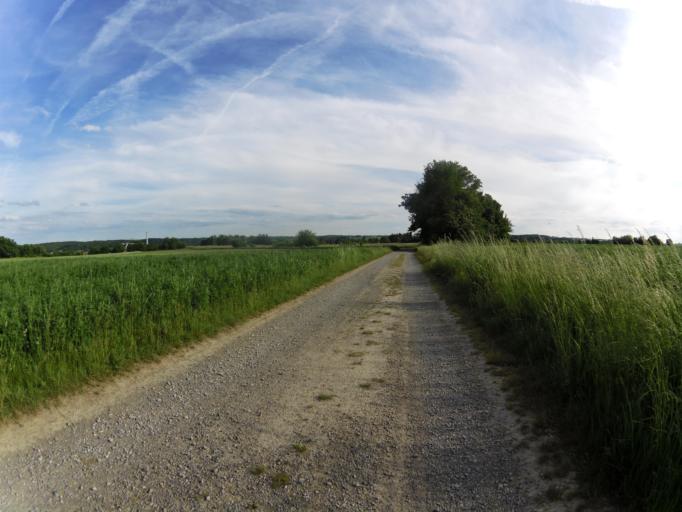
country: DE
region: Bavaria
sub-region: Regierungsbezirk Unterfranken
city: Ochsenfurt
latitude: 49.6762
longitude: 10.0711
